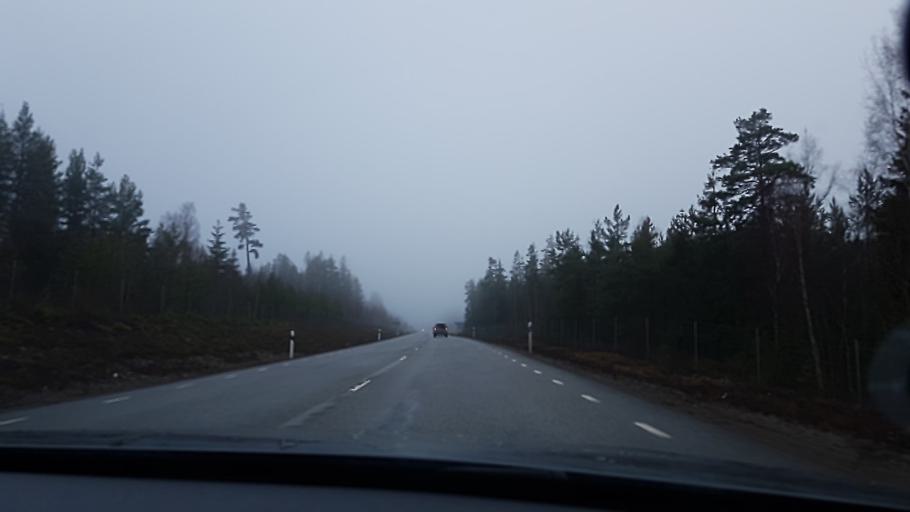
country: SE
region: Vaestra Goetaland
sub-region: Gullspangs Kommun
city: Gullspang
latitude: 58.8940
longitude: 14.0168
